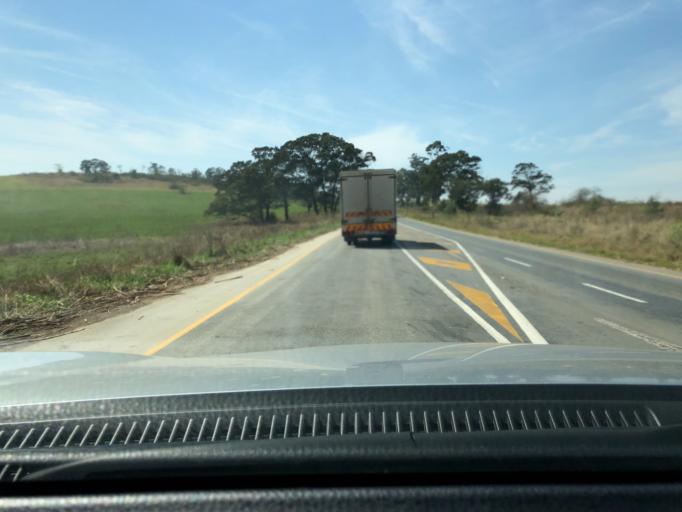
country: ZA
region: KwaZulu-Natal
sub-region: uMgungundlovu District Municipality
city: Camperdown
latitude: -29.7226
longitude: 30.4775
